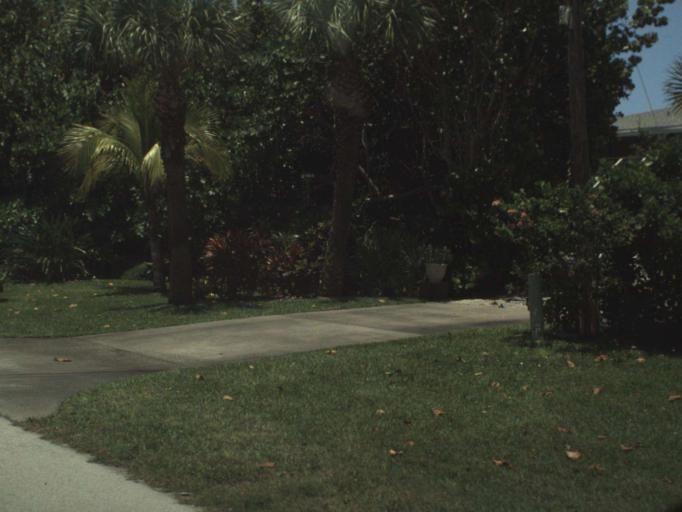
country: US
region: Florida
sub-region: Brevard County
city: Micco
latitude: 27.9142
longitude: -80.4782
